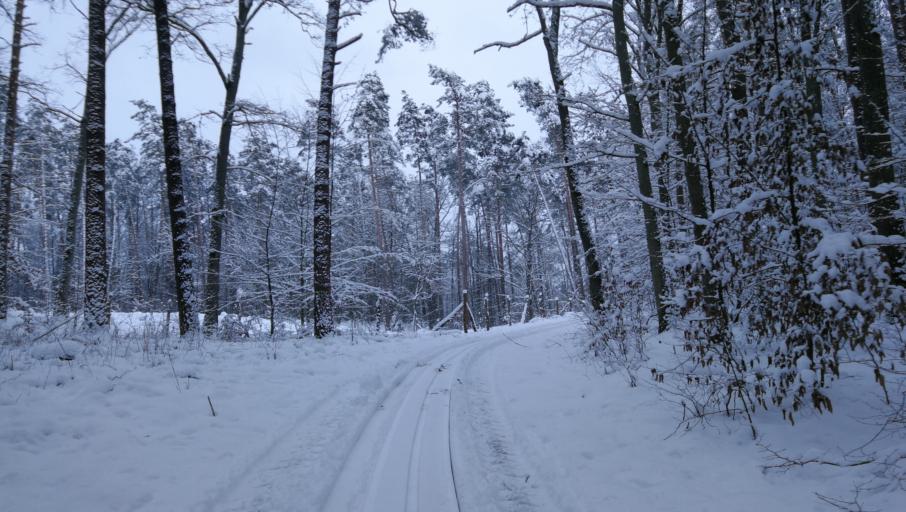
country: PL
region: Kujawsko-Pomorskie
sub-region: Powiat brodnicki
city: Gorzno
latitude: 53.2025
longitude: 19.6982
